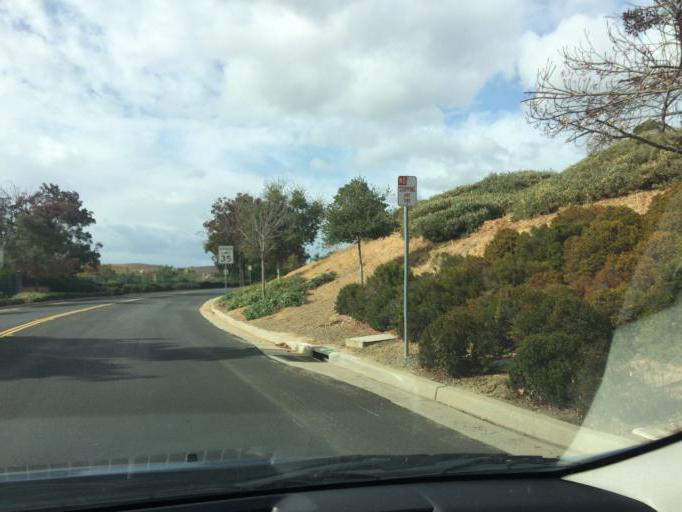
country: US
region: California
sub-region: Santa Clara County
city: Seven Trees
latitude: 37.2805
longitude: -121.7610
